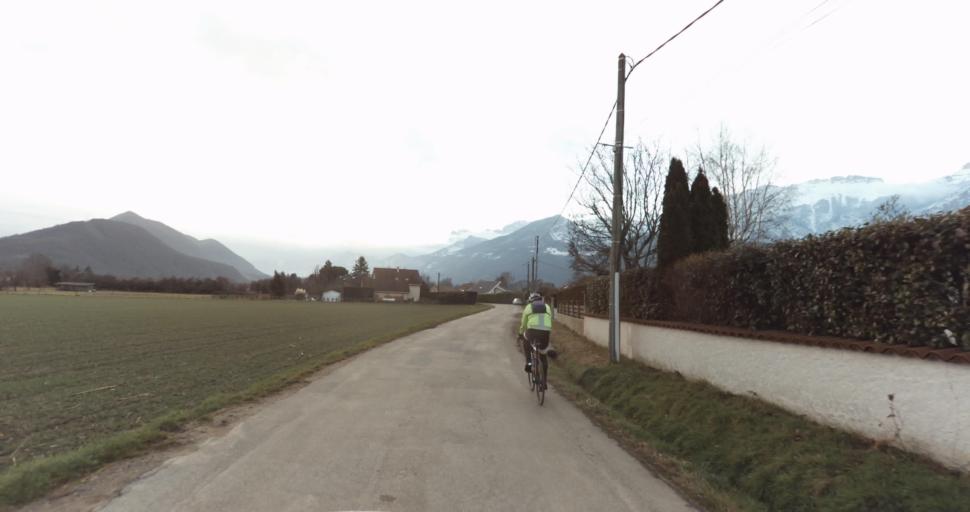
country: FR
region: Rhone-Alpes
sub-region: Departement de l'Isere
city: Vif
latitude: 45.0730
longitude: 5.6981
